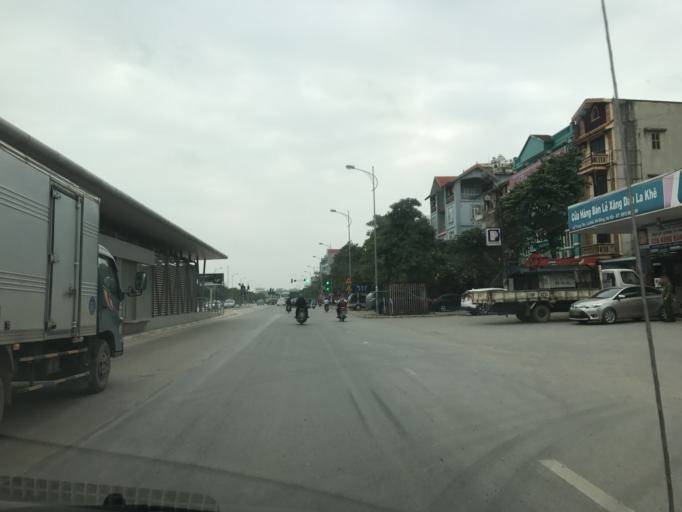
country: VN
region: Ha Noi
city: Ha Dong
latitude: 20.9654
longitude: 105.7598
